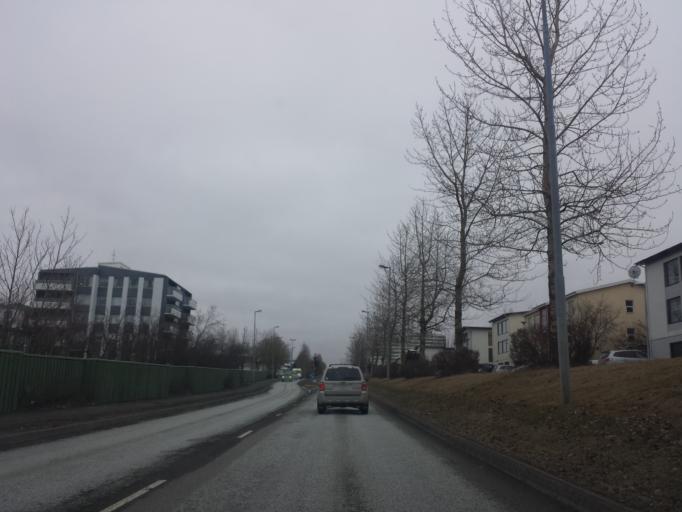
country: IS
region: Capital Region
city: Reykjavik
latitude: 64.1140
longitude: -21.8787
